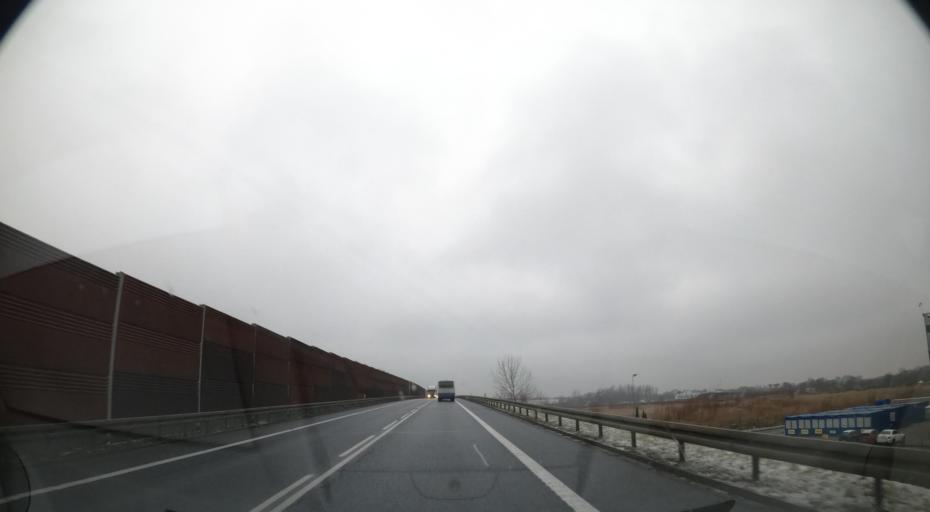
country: PL
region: Masovian Voivodeship
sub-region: Powiat sochaczewski
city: Sochaczew
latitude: 52.2206
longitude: 20.2590
